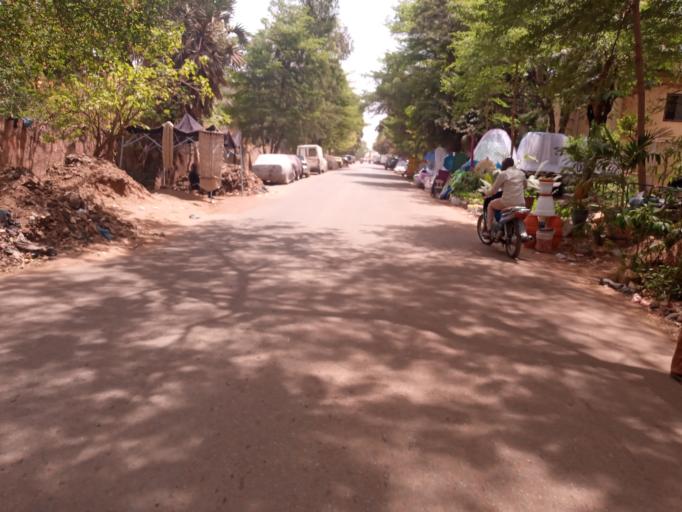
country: ML
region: Bamako
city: Bamako
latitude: 12.6384
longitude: -7.9949
